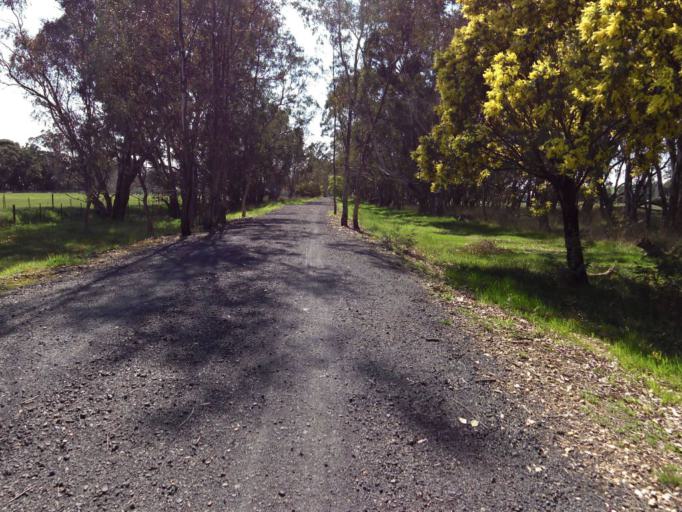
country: AU
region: Victoria
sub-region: Murrindindi
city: Alexandra
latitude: -37.1083
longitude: 145.6137
